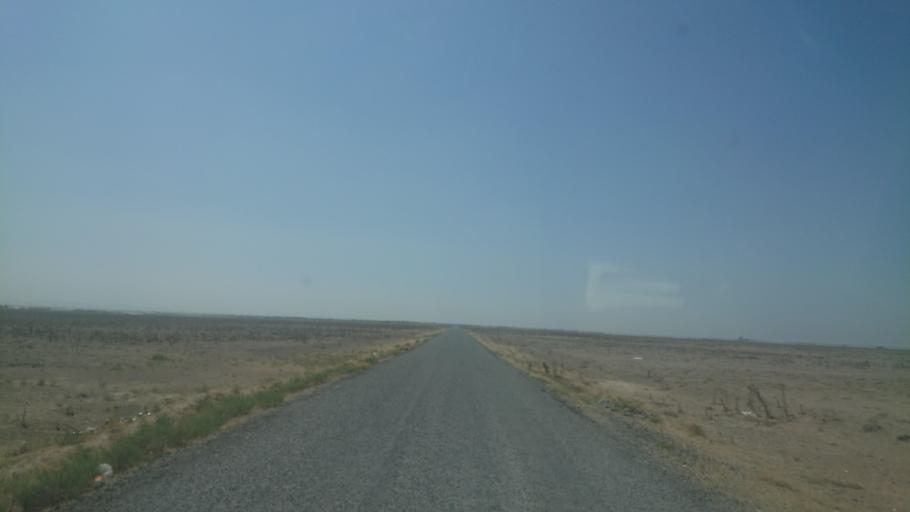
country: TR
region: Aksaray
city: Yesilova
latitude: 38.3235
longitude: 33.7451
